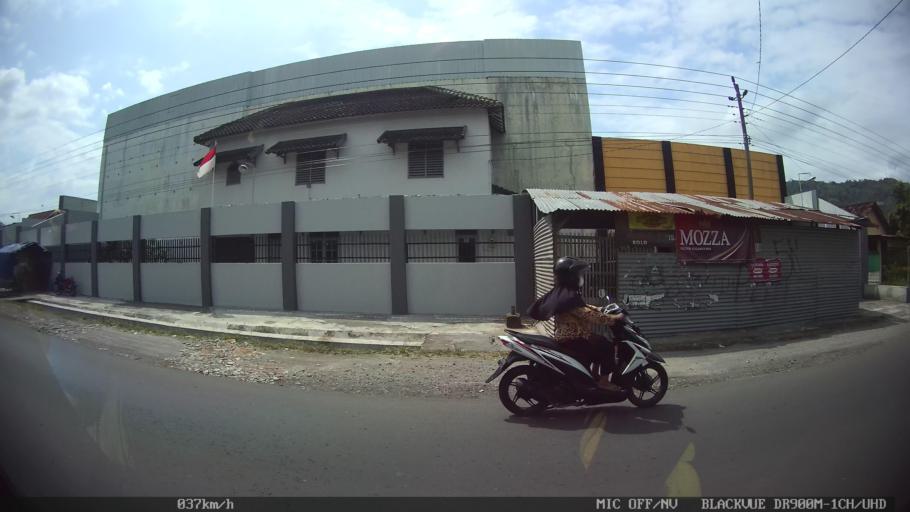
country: ID
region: Daerah Istimewa Yogyakarta
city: Depok
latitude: -7.8338
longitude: 110.4772
